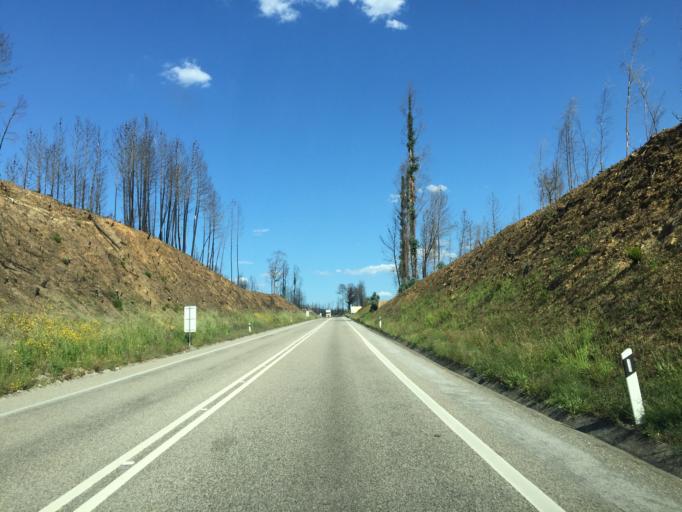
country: PT
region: Leiria
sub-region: Pedrogao Grande
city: Pedrogao Grande
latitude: 39.9270
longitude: -8.1787
